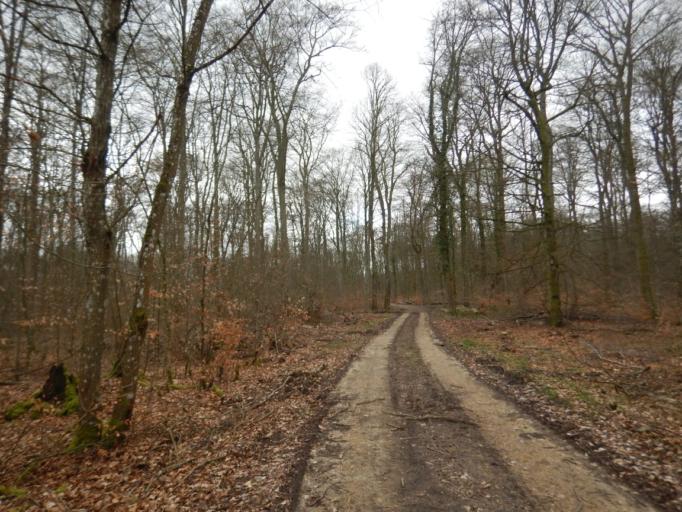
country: LU
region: Luxembourg
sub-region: Canton de Mersch
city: Tuntange
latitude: 49.7285
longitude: 6.0427
